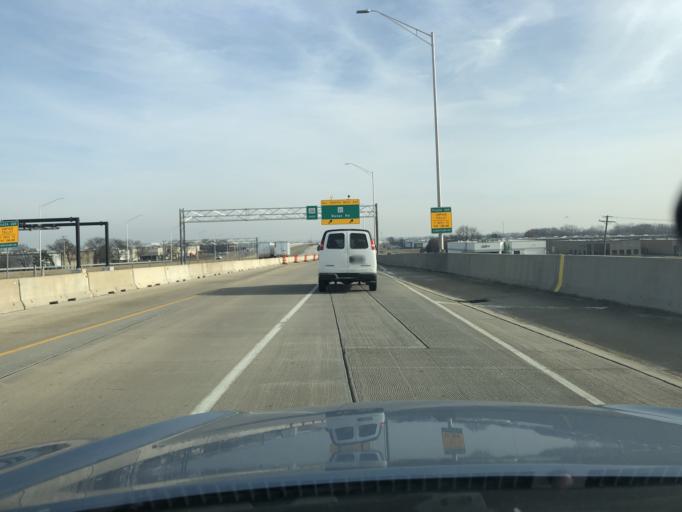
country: US
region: Illinois
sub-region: Cook County
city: Elk Grove Village
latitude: 41.9831
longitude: -87.9694
